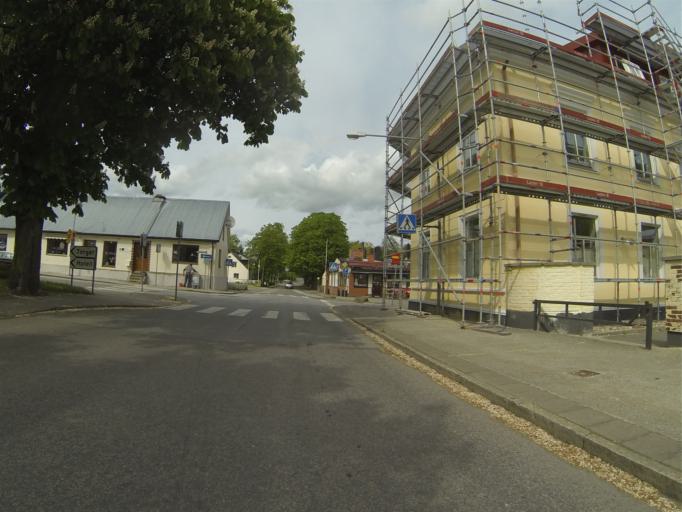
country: SE
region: Skane
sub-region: Tomelilla Kommun
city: Tomelilla
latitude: 55.5436
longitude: 13.9551
